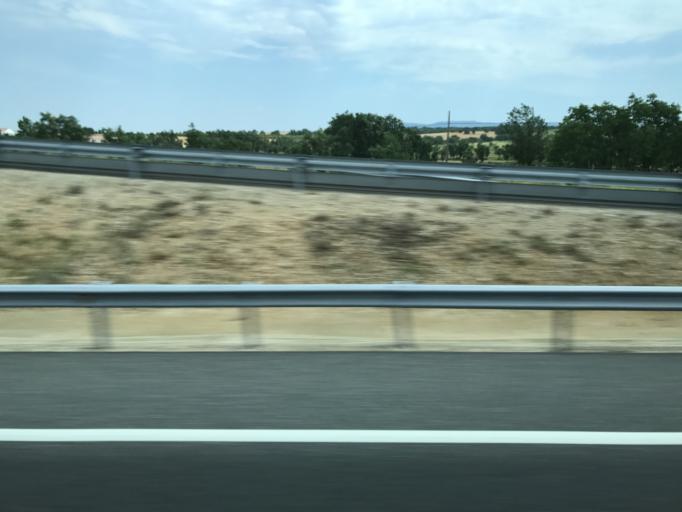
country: ES
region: Castille and Leon
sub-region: Provincia de Segovia
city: Castillejo de Mesleon
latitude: 41.2570
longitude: -3.5934
